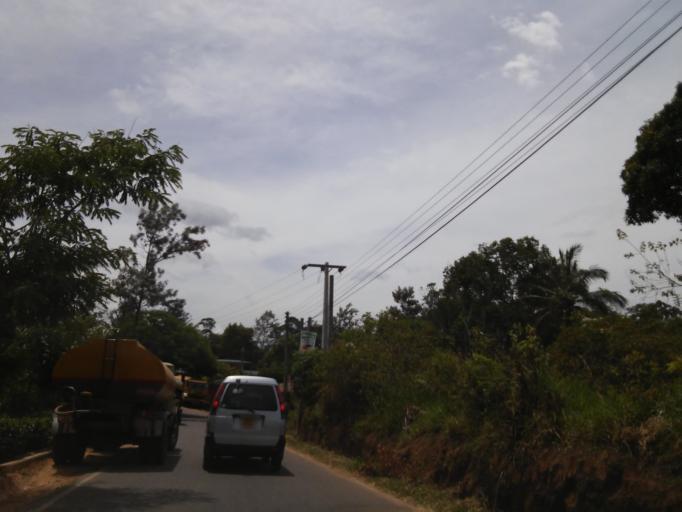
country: LK
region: Uva
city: Haputale
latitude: 6.8420
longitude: 81.0160
